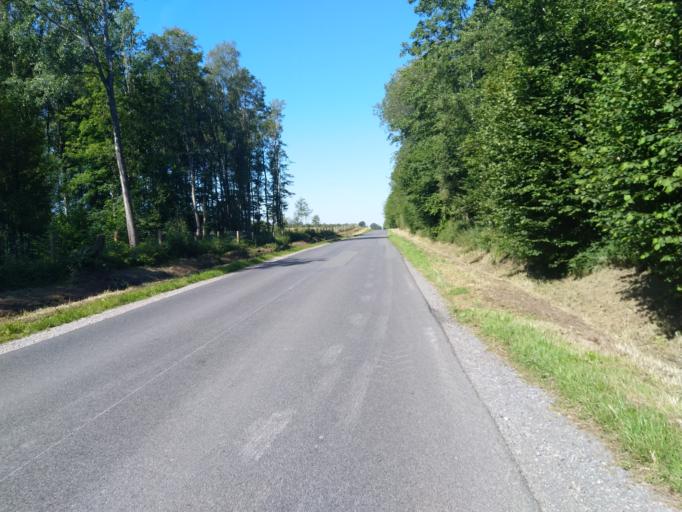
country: FR
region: Nord-Pas-de-Calais
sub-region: Departement du Nord
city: Feignies
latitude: 50.3223
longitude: 3.8862
